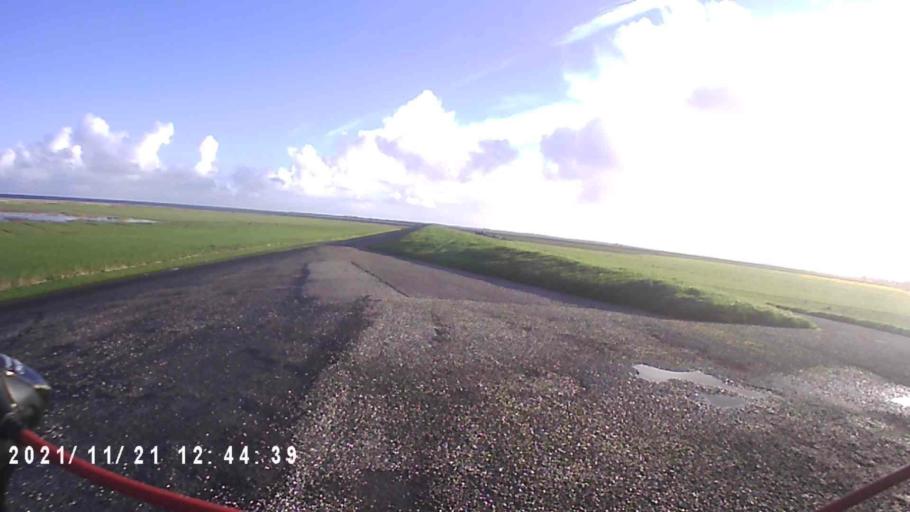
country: NL
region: Friesland
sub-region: Gemeente Dongeradeel
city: Anjum
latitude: 53.4007
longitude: 6.1012
